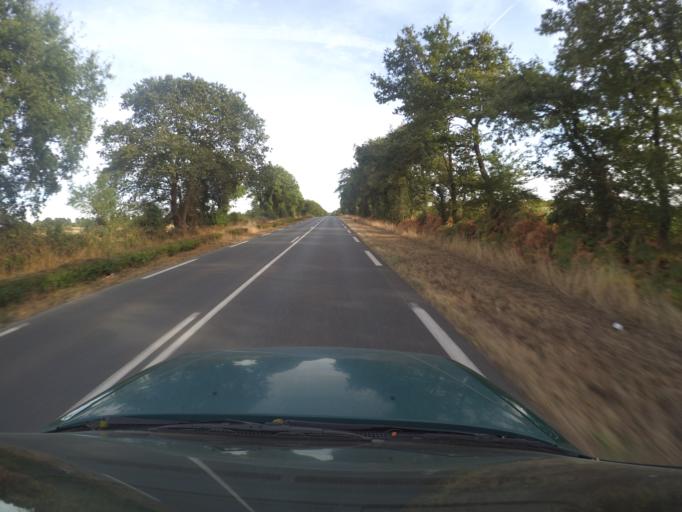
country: FR
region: Pays de la Loire
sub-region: Departement de la Vendee
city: Saint-Hilaire-de-Loulay
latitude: 46.9909
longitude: -1.3240
